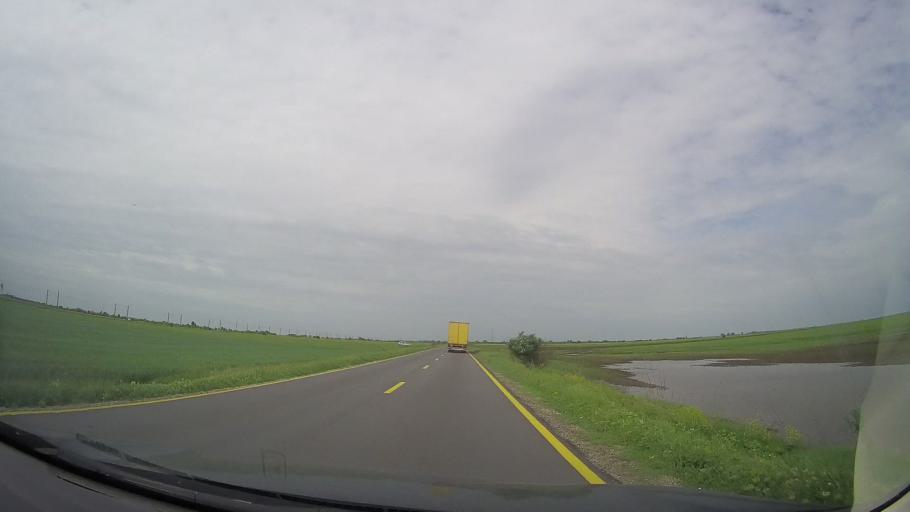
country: RO
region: Olt
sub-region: Comuna Mihaesti
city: Busca
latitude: 44.1243
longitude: 24.8201
